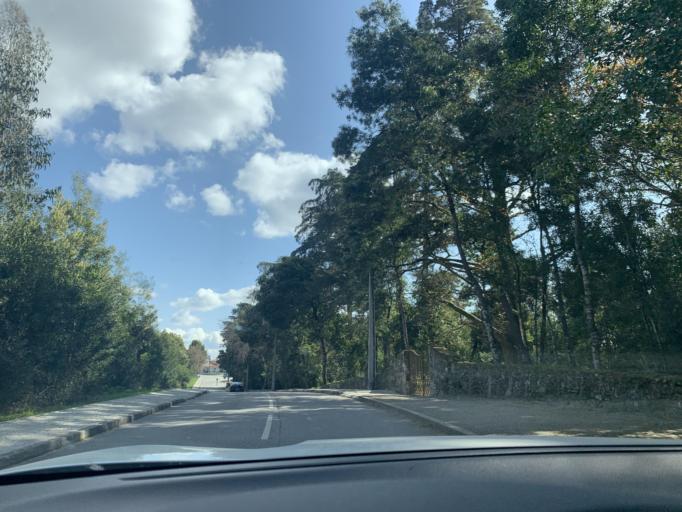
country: PT
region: Viseu
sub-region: Viseu
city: Rio de Loba
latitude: 40.6968
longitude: -7.8665
